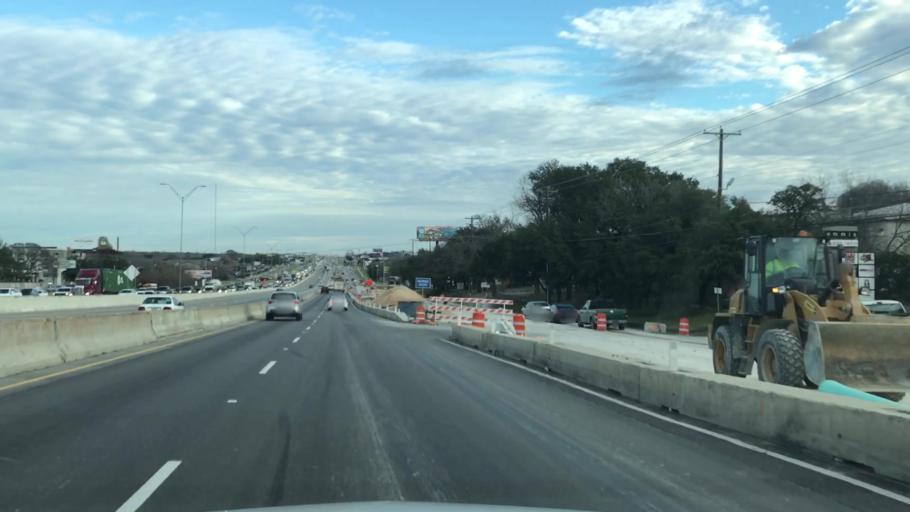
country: US
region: Texas
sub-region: Travis County
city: Austin
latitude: 30.3457
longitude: -97.6956
